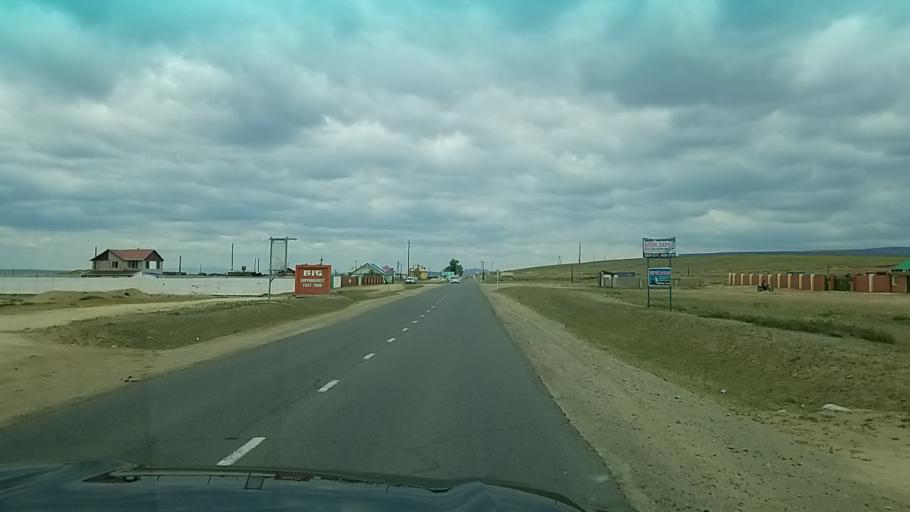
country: MN
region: Darhan Uul
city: Darhan
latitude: 49.3950
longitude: 105.9327
